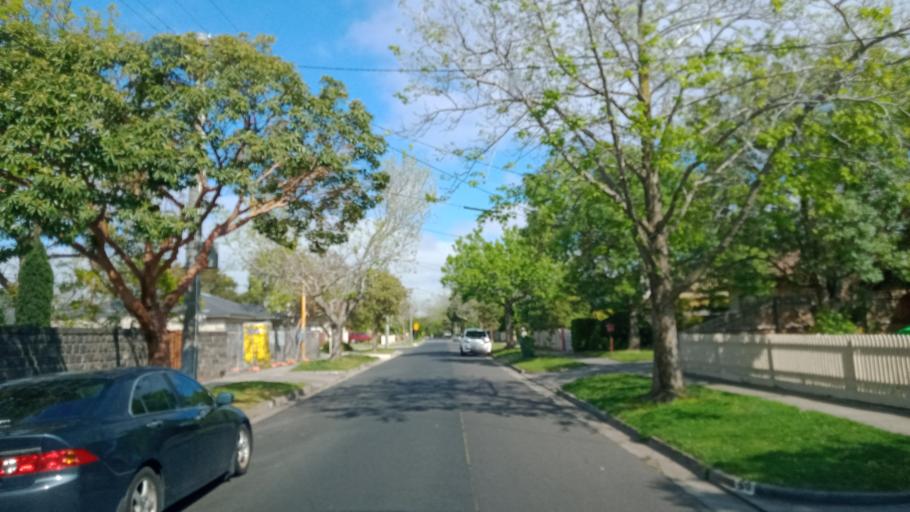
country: AU
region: Victoria
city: Hughesdale
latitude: -37.9128
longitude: 145.0813
